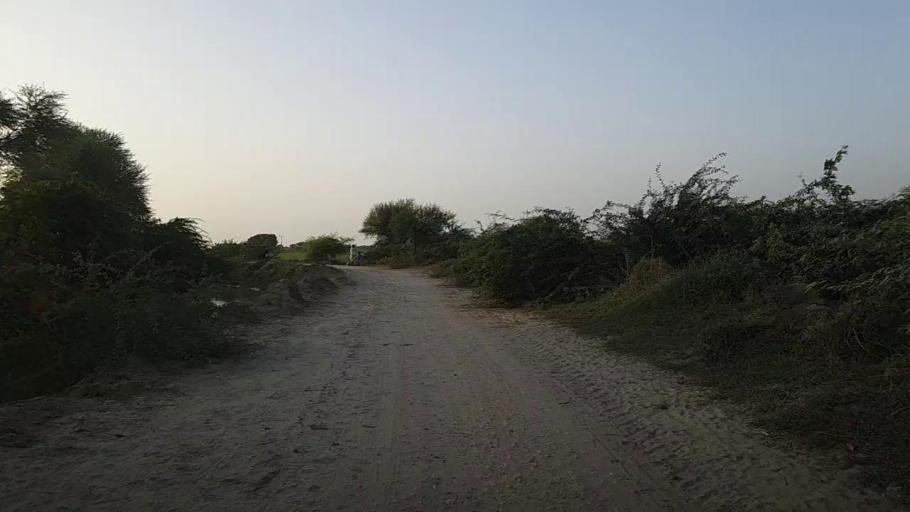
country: PK
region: Sindh
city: Kario
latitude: 24.7077
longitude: 68.4648
